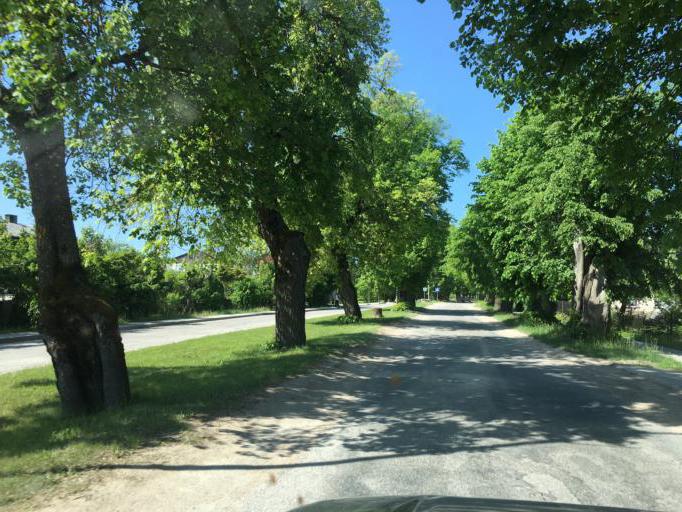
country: LV
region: Dundaga
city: Dundaga
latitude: 57.5058
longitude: 22.3502
